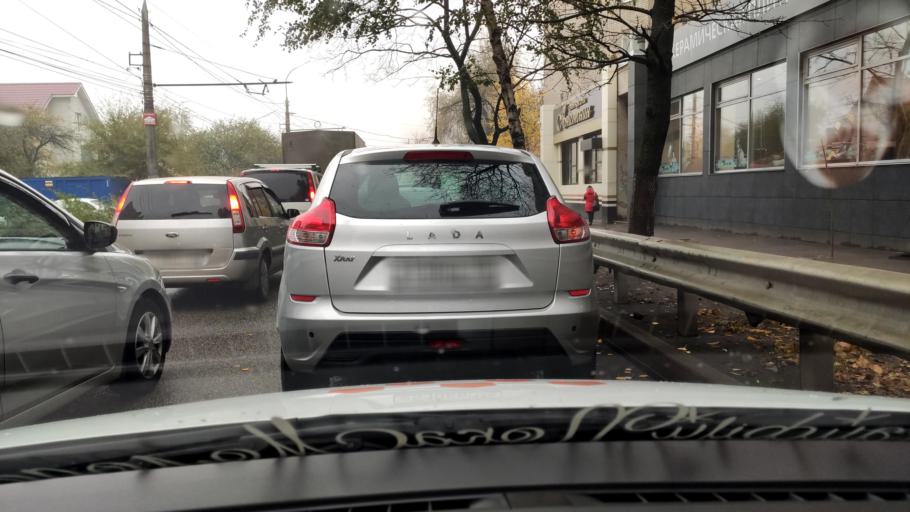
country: RU
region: Voronezj
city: Voronezh
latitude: 51.7032
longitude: 39.1949
